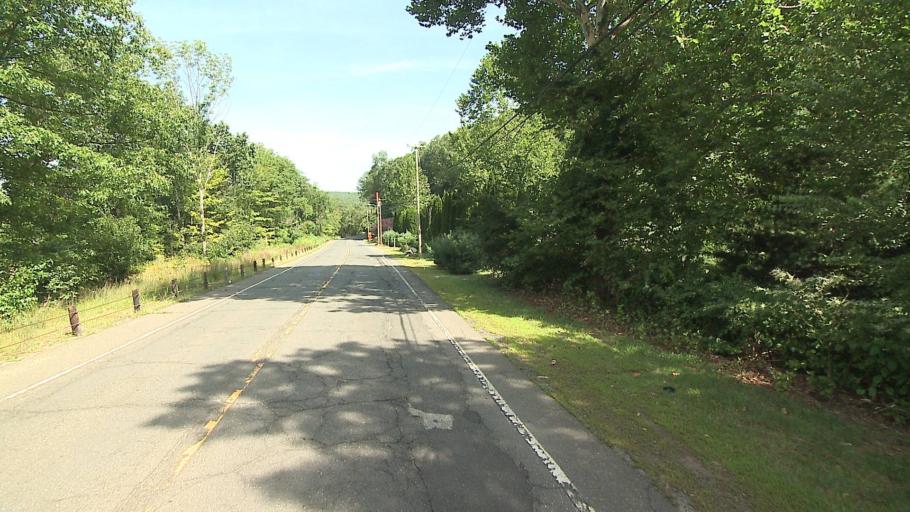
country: US
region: Connecticut
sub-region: Litchfield County
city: Oakville
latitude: 41.6127
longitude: -73.0579
